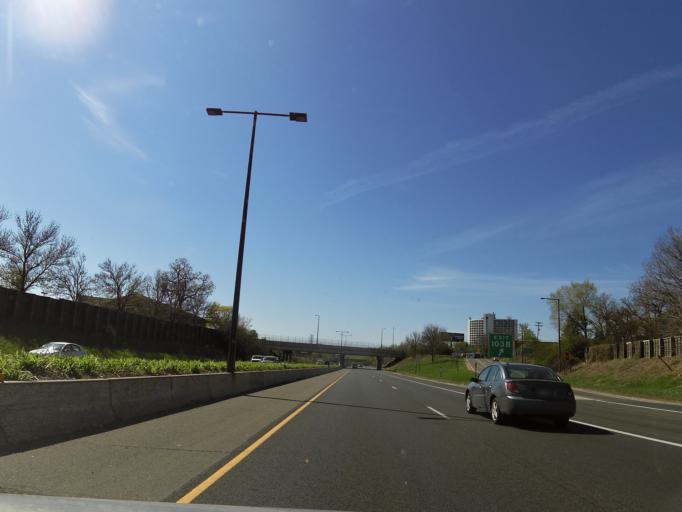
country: US
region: Minnesota
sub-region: Dakota County
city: Mendota Heights
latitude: 44.9180
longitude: -93.1445
